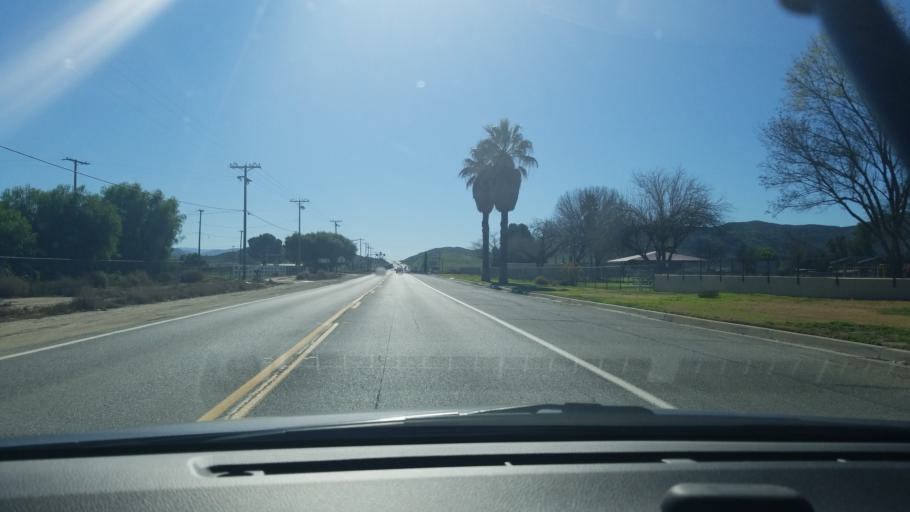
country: US
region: California
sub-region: Riverside County
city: Winchester
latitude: 33.7033
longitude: -117.0849
